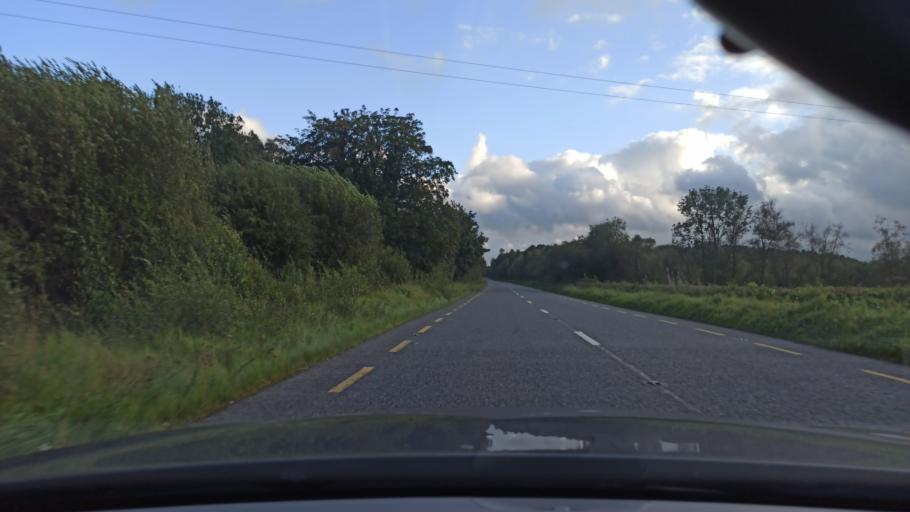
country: IE
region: Munster
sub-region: North Tipperary
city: Templemore
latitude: 52.8713
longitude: -7.8107
